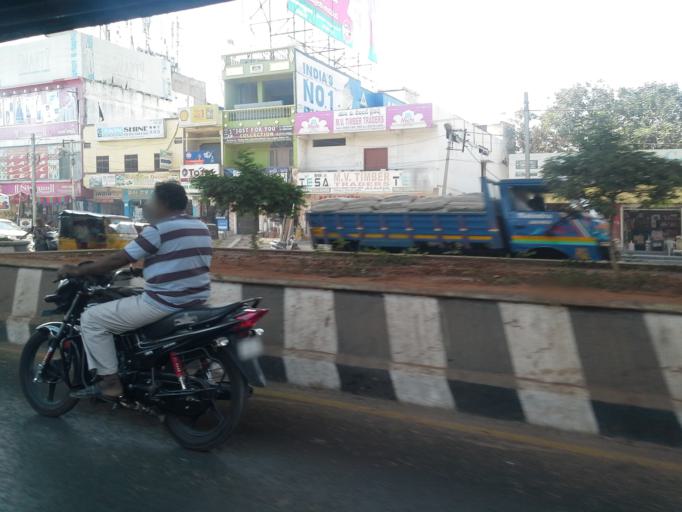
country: IN
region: Telangana
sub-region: Hyderabad
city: Hyderabad
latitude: 17.3778
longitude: 78.4294
